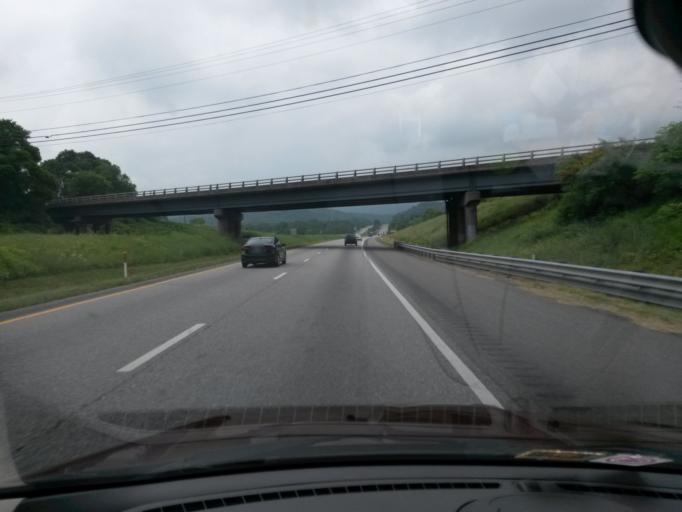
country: US
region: Virginia
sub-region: City of Waynesboro
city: Waynesboro
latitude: 38.0538
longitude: -78.9196
